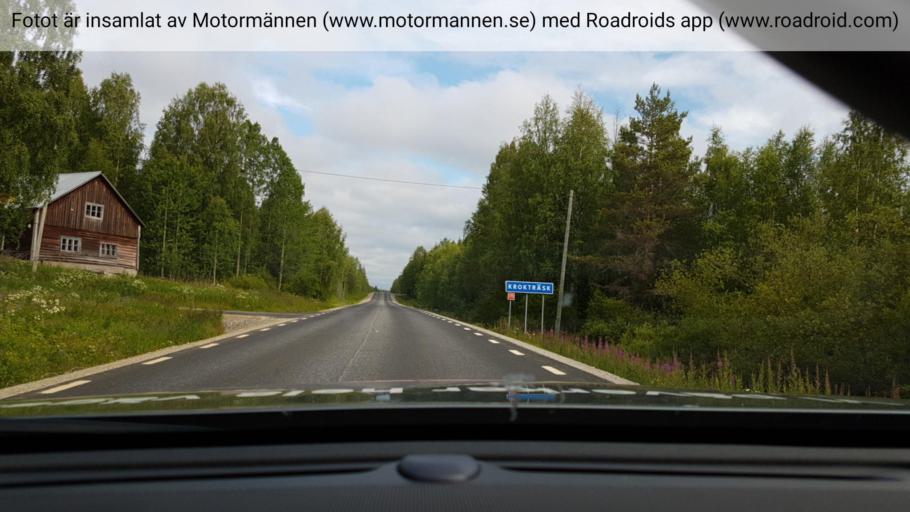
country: SE
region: Vaesterbotten
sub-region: Vindelns Kommun
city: Vindeln
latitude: 64.4509
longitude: 19.3391
